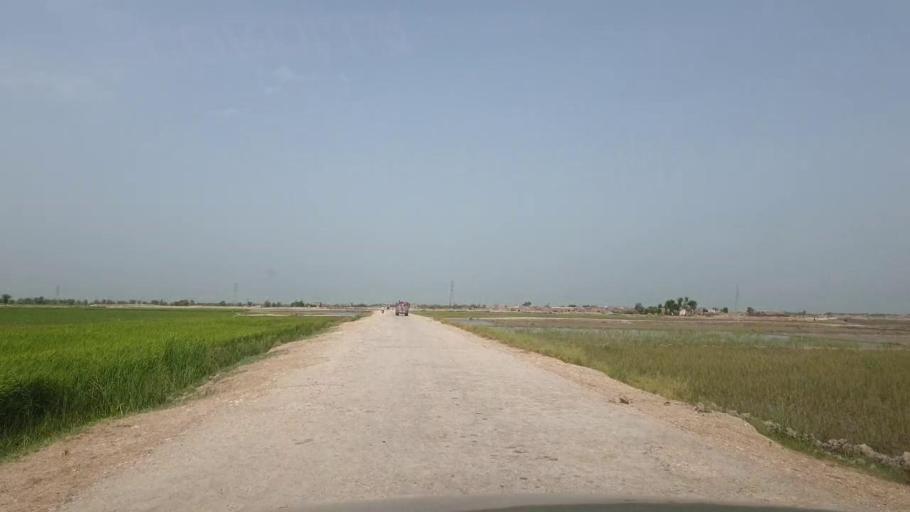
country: PK
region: Sindh
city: Garhi Yasin
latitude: 27.8541
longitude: 68.4322
